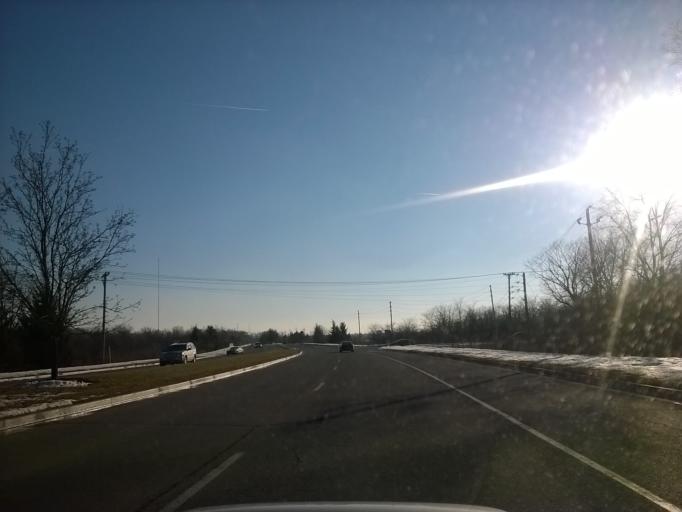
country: US
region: Indiana
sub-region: Hamilton County
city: Carmel
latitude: 39.9423
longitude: -86.0744
